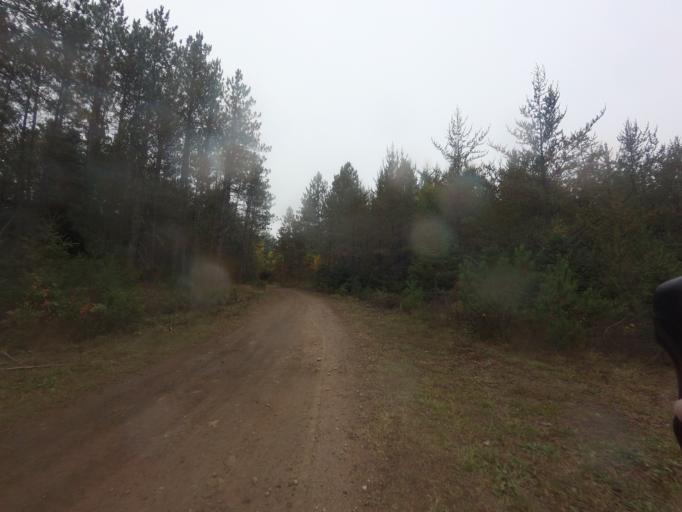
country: CA
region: Ontario
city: Petawawa
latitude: 45.7757
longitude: -77.3784
